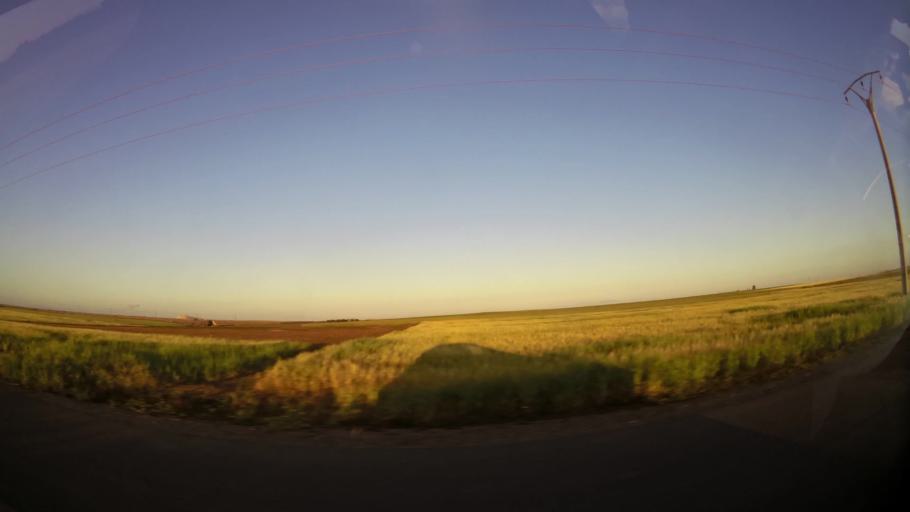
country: MA
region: Marrakech-Tensift-Al Haouz
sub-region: Kelaa-Des-Sraghna
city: Sidi Abdallah
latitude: 32.2343
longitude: -7.9288
